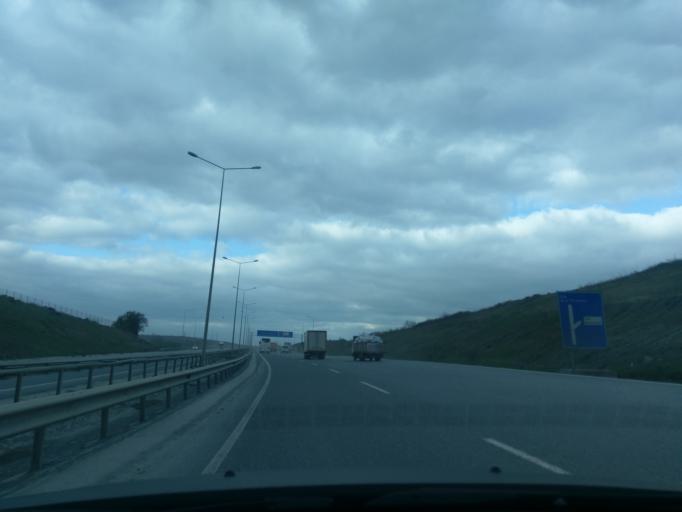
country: TR
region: Istanbul
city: Kemerburgaz
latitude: 41.2308
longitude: 28.8266
